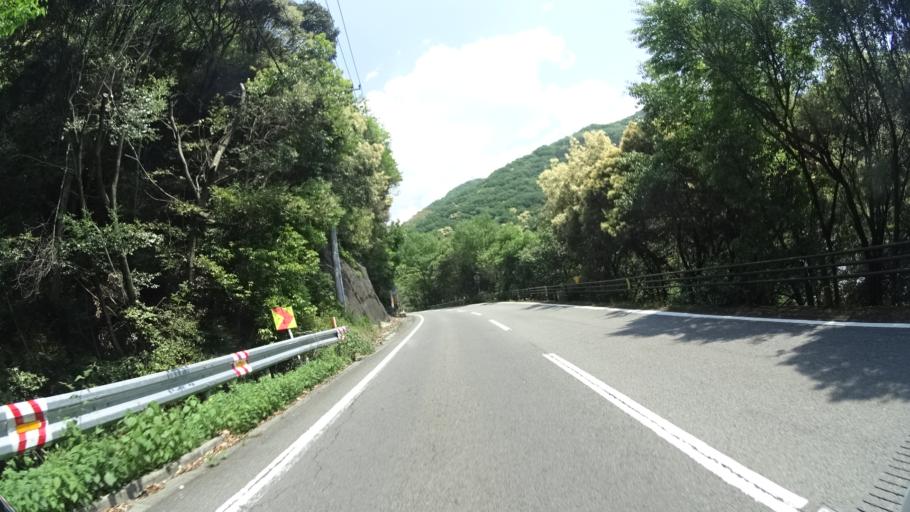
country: JP
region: Ehime
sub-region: Shikoku-chuo Shi
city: Matsuyama
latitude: 33.8732
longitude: 132.8309
